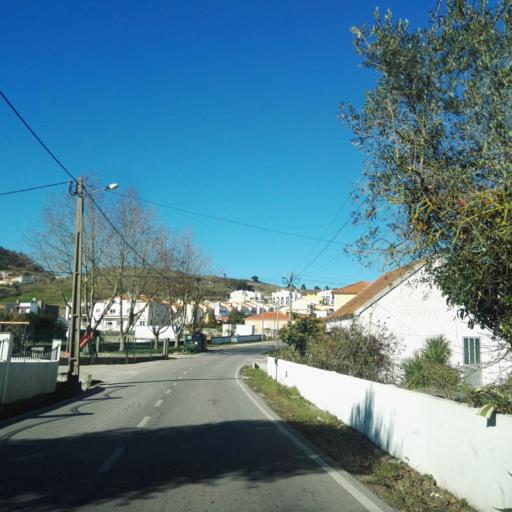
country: PT
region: Lisbon
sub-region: Mafra
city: Venda do Pinheiro
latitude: 38.9488
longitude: -9.2329
